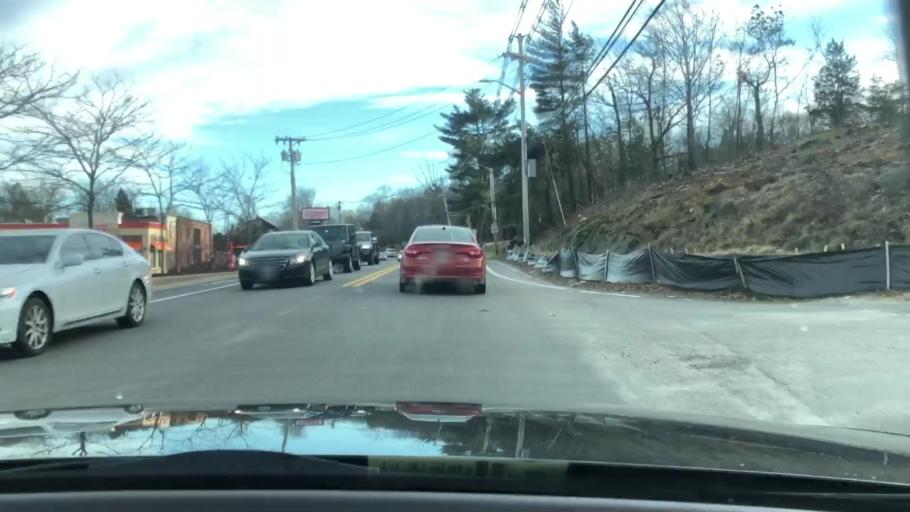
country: US
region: Massachusetts
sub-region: Worcester County
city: Milford
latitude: 42.1253
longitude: -71.5171
